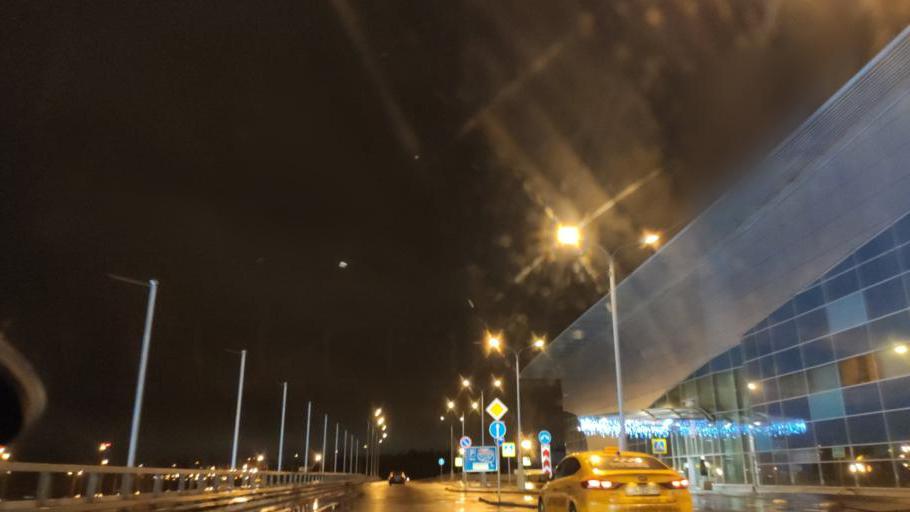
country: RU
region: Moskovskaya
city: Novopodrezkovo
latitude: 55.9622
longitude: 37.4054
